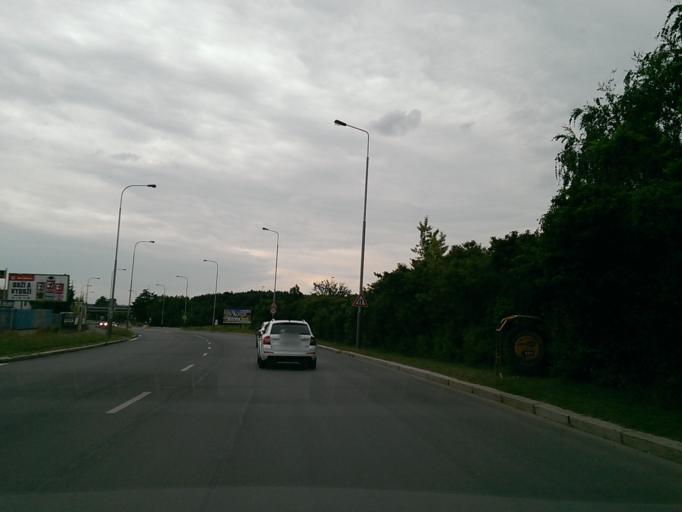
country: CZ
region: Praha
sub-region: Praha 14
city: Dolni Pocernice
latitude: 50.0465
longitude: 14.5669
